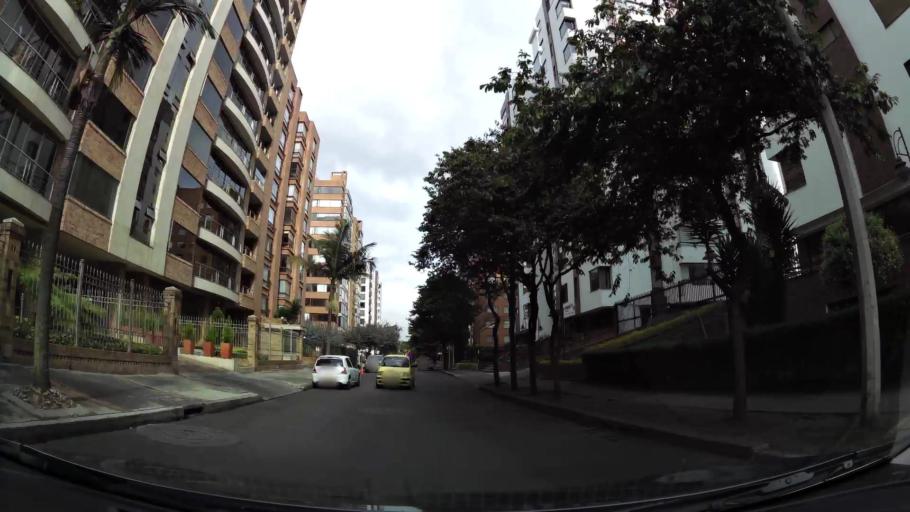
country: CO
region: Bogota D.C.
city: Barrio San Luis
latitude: 4.7031
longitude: -74.0346
